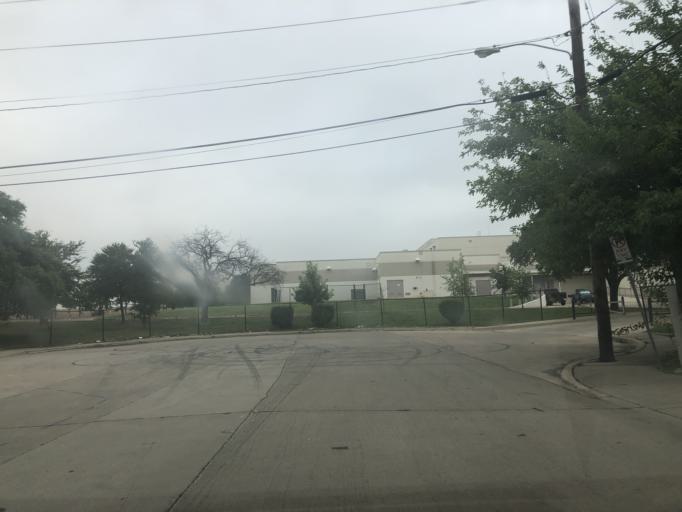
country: US
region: Texas
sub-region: Dallas County
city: Farmers Branch
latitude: 32.8714
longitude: -96.8768
